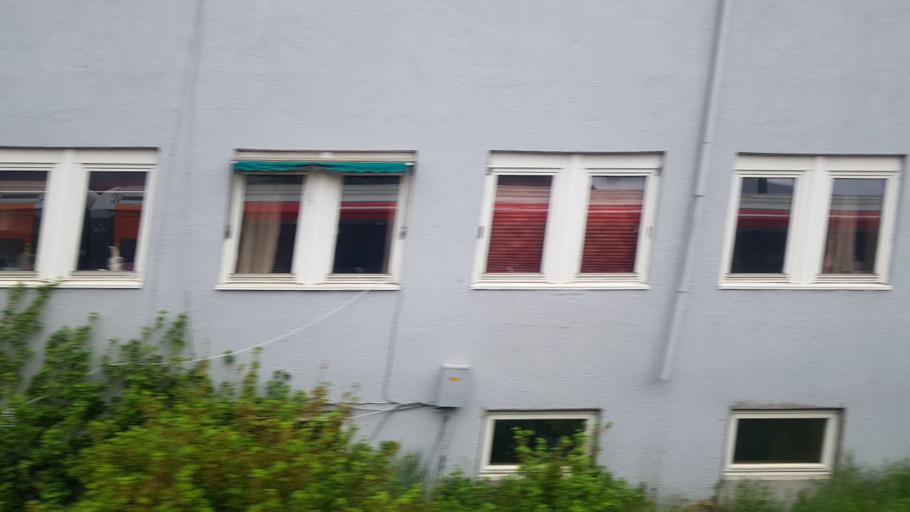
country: NO
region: Oppland
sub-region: Sor-Fron
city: Hundorp
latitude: 61.5633
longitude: 9.9191
